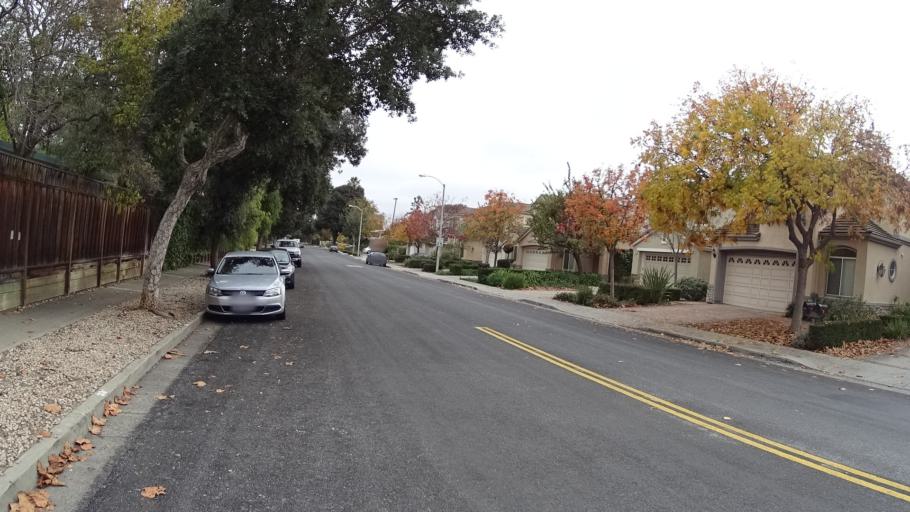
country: US
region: California
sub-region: Santa Clara County
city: Sunnyvale
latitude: 37.3544
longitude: -122.0414
